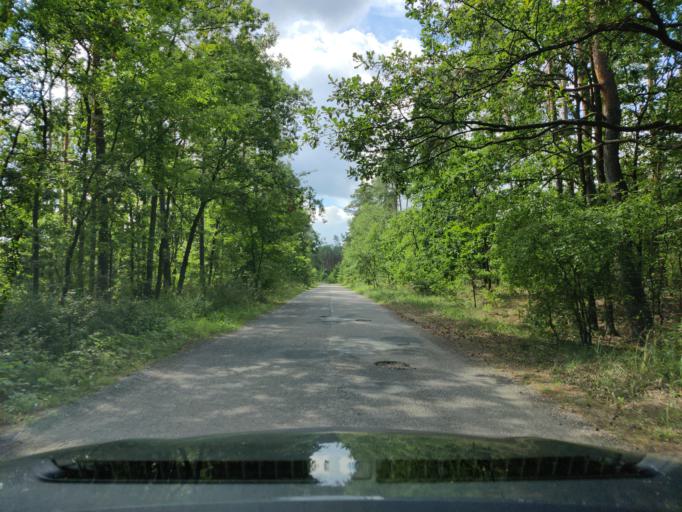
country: PL
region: Masovian Voivodeship
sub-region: Powiat pultuski
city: Pultusk
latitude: 52.7243
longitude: 21.1297
